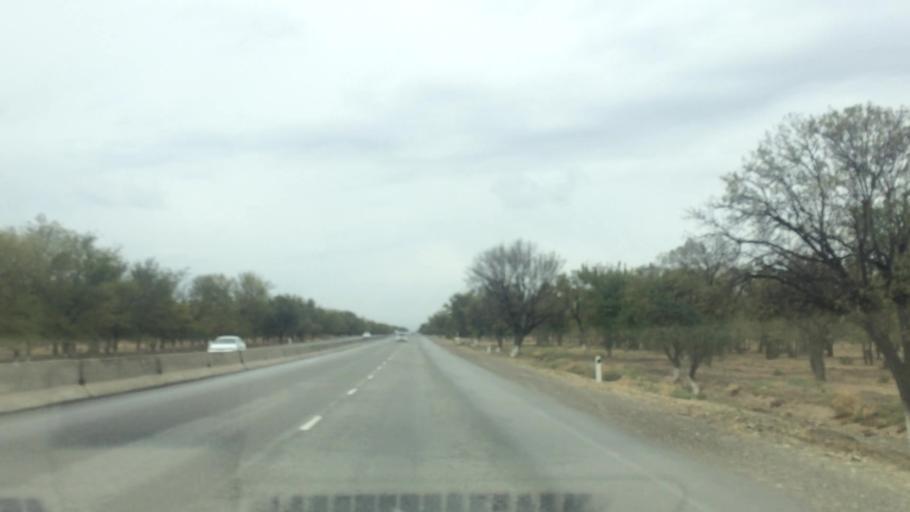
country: UZ
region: Samarqand
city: Bulung'ur
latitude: 39.8287
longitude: 67.4079
